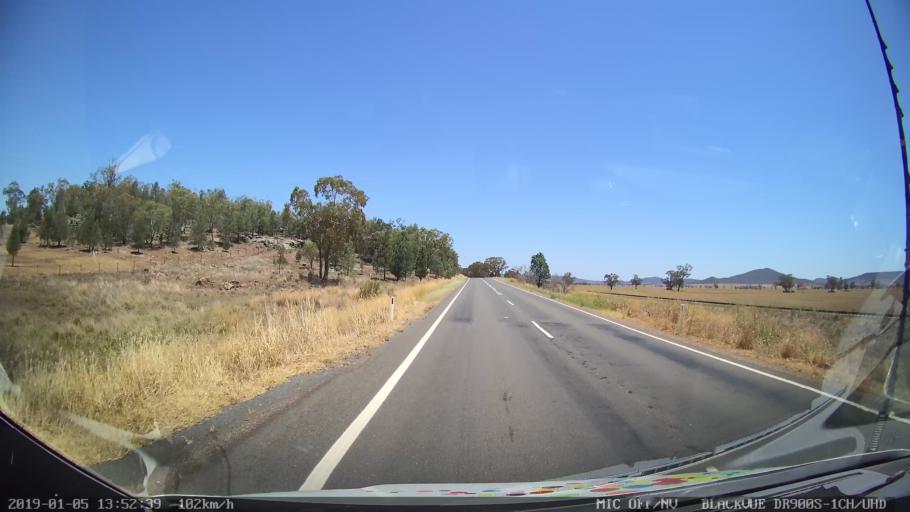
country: AU
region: New South Wales
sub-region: Gunnedah
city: Gunnedah
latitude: -31.0631
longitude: 150.2770
